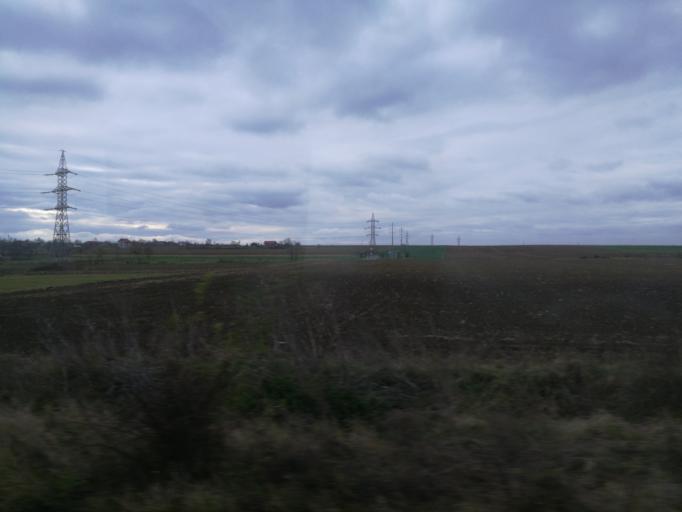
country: RO
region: Iasi
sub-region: Comuna Halaucesti
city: Halaucesti
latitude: 47.1071
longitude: 26.8044
